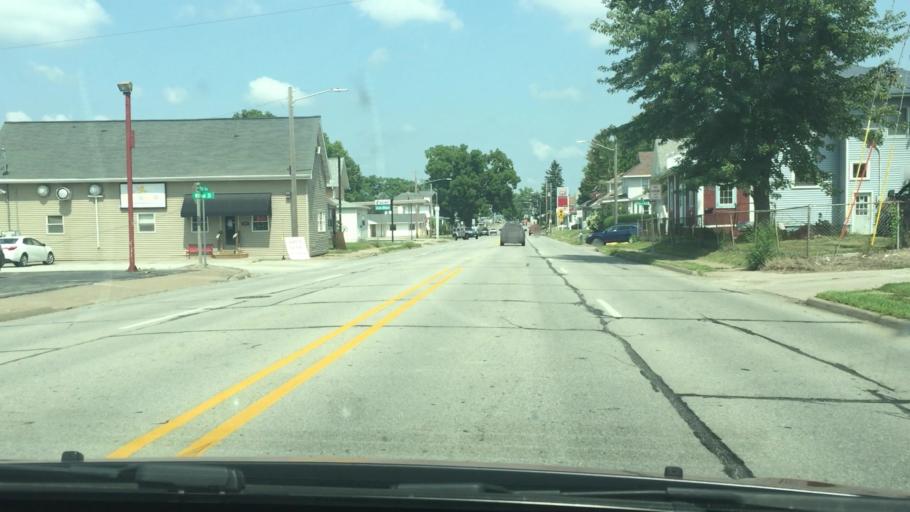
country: US
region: Iowa
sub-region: Muscatine County
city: Muscatine
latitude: 41.4314
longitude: -91.0311
